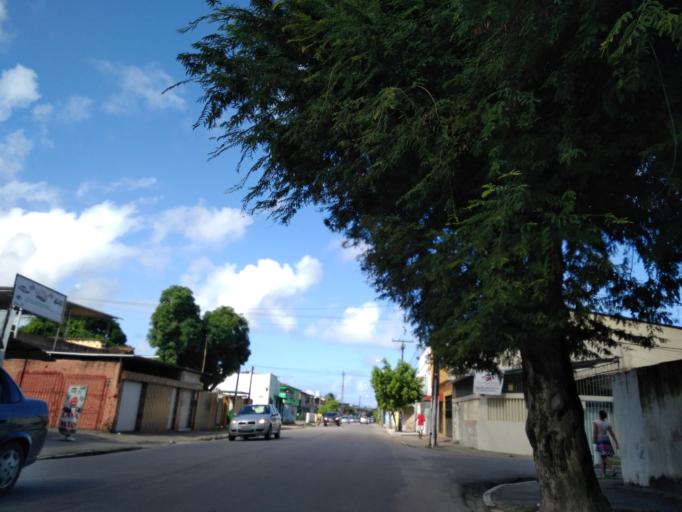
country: BR
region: Pernambuco
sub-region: Recife
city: Recife
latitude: -8.0766
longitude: -34.9128
